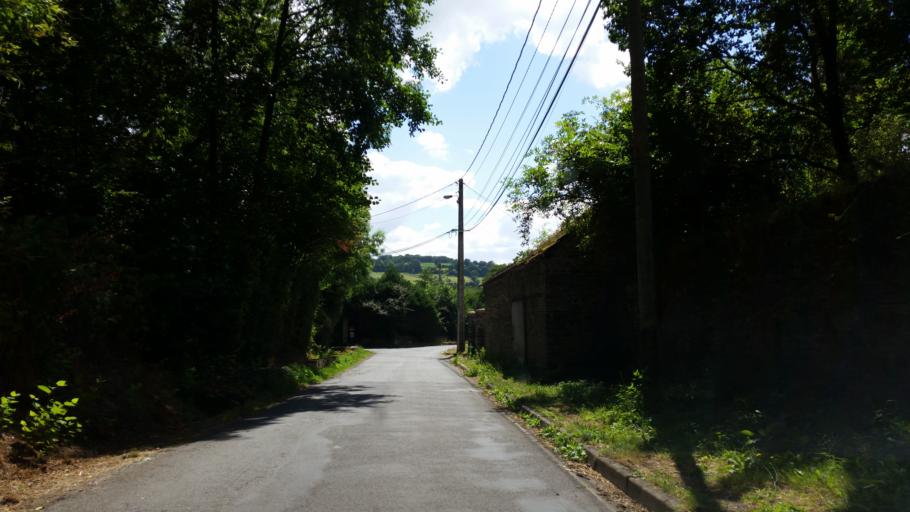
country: FR
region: Lower Normandy
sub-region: Departement du Calvados
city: Clecy
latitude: 48.8505
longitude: -0.3816
